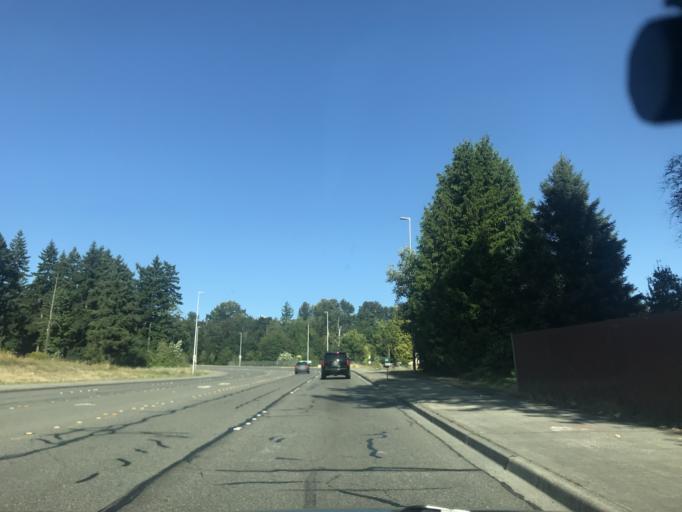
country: US
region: Washington
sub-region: King County
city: Lea Hill
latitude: 47.3561
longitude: -122.1913
